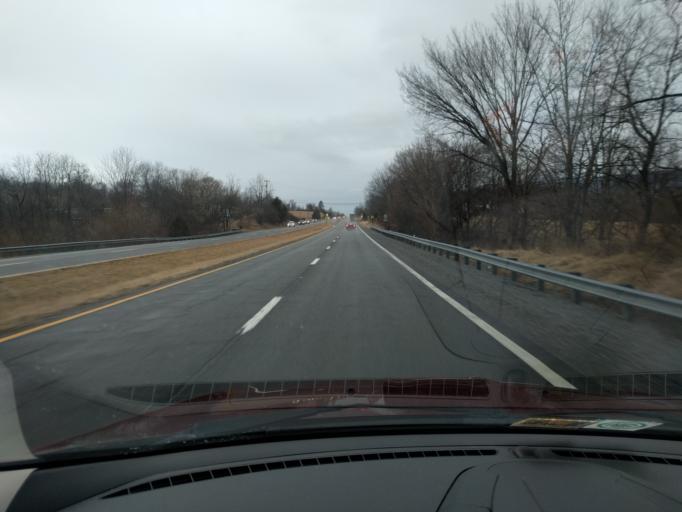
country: US
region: Virginia
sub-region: Giles County
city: Pembroke
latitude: 37.3090
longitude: -80.5774
